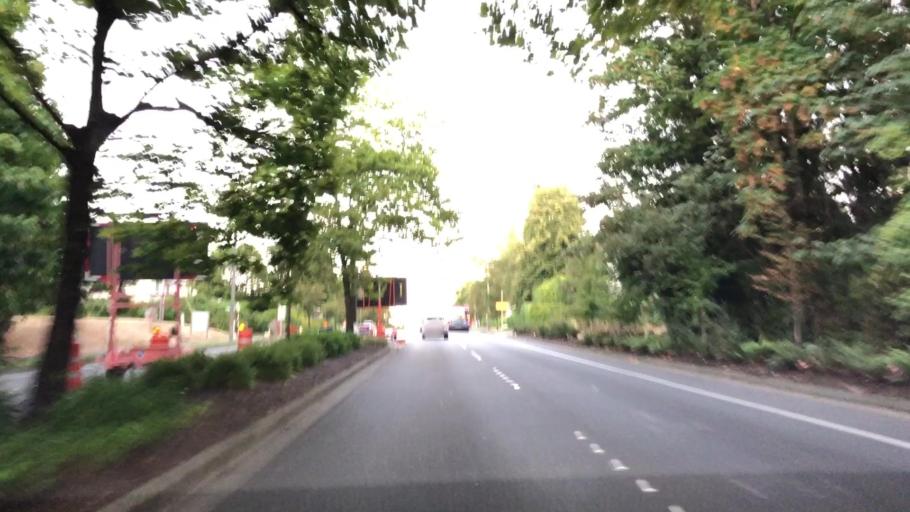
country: US
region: Washington
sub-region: King County
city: Bellevue
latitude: 47.6171
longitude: -122.1601
